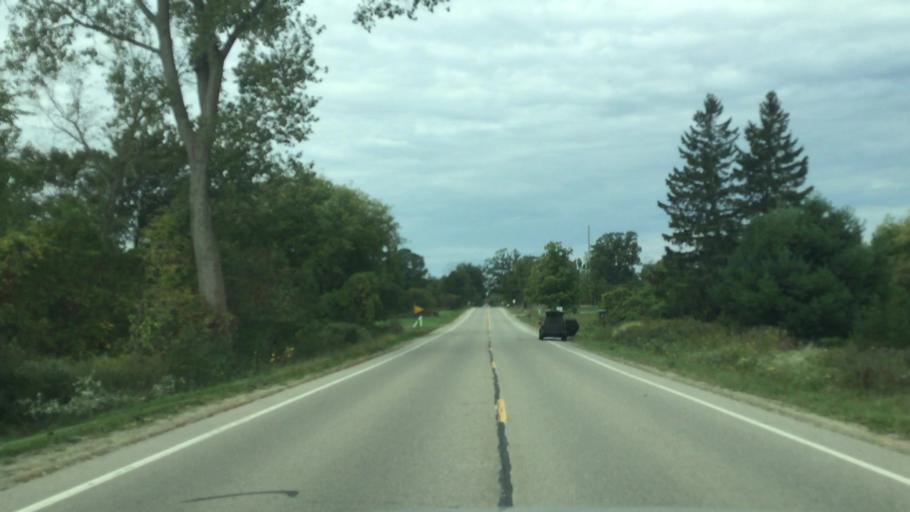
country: US
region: Michigan
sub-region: Livingston County
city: Howell
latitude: 42.6741
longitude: -83.8688
